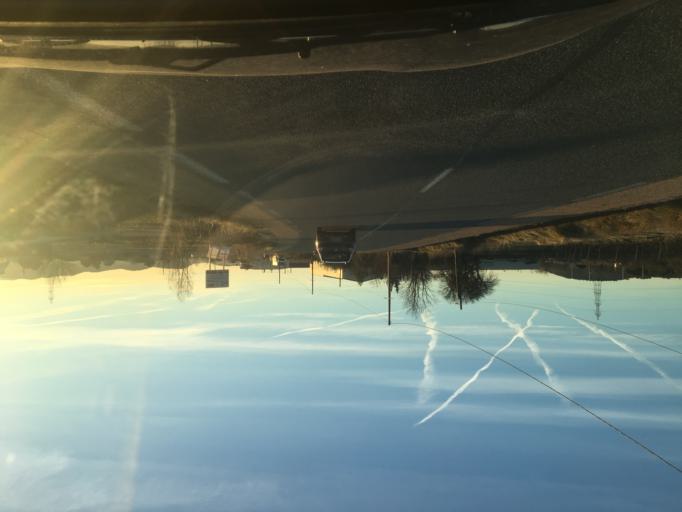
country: FR
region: Provence-Alpes-Cote d'Azur
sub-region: Departement du Var
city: Les Arcs
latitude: 43.4506
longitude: 6.4597
